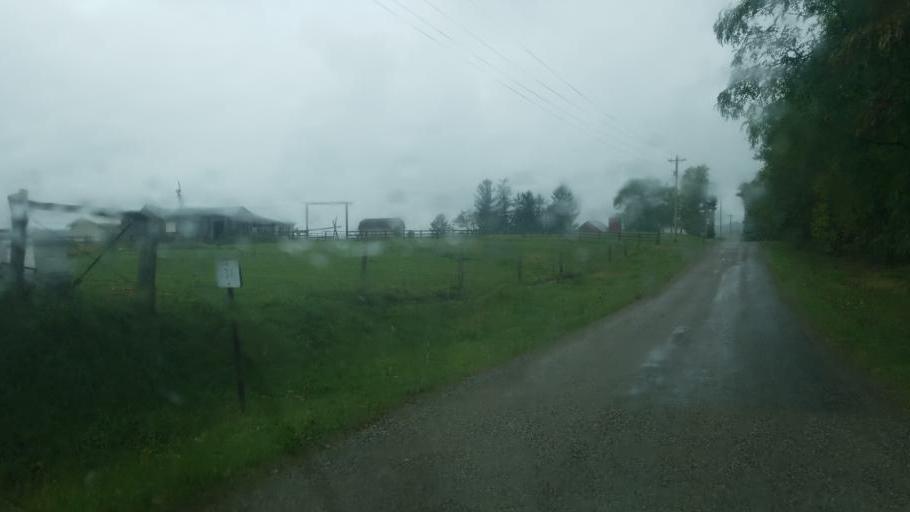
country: US
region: Ohio
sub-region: Holmes County
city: Millersburg
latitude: 40.5839
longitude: -81.8587
